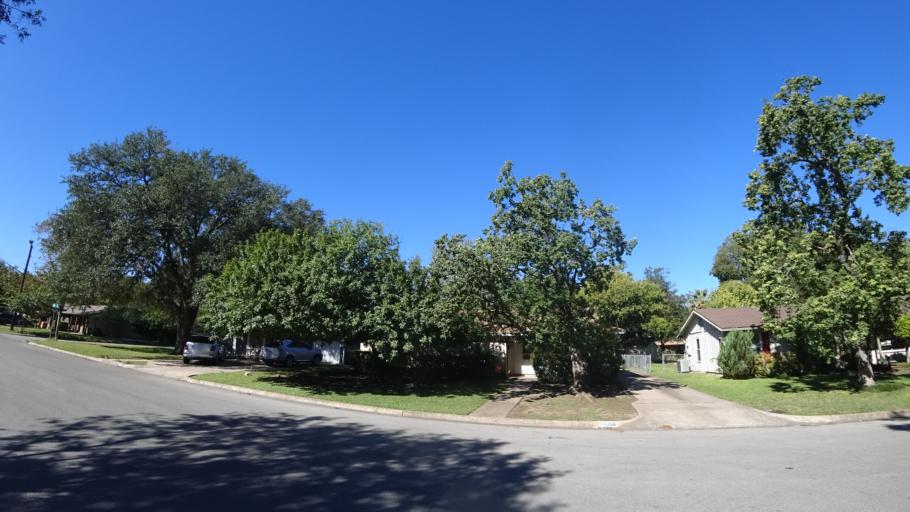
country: US
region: Texas
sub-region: Travis County
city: Austin
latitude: 30.3039
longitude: -97.6893
